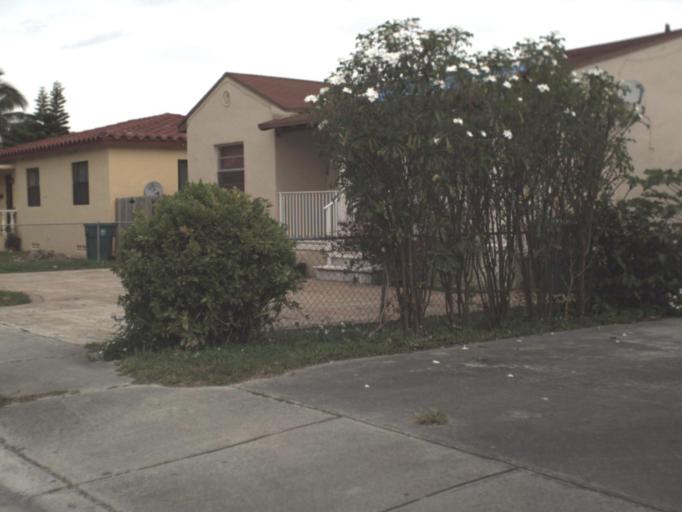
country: US
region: Florida
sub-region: Miami-Dade County
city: Brownsville
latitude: 25.7903
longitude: -80.2559
